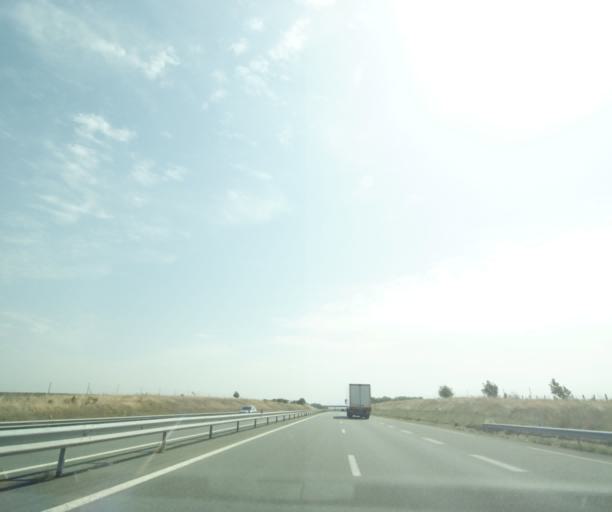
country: FR
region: Pays de la Loire
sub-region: Departement de la Vendee
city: Fontenay-le-Comte
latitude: 46.4516
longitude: -0.8601
